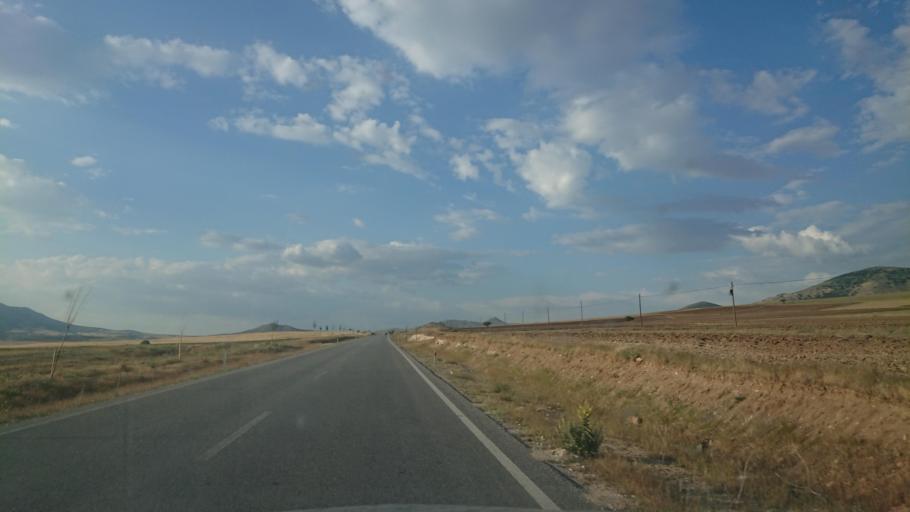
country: TR
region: Aksaray
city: Aksaray
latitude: 38.5320
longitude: 34.0976
